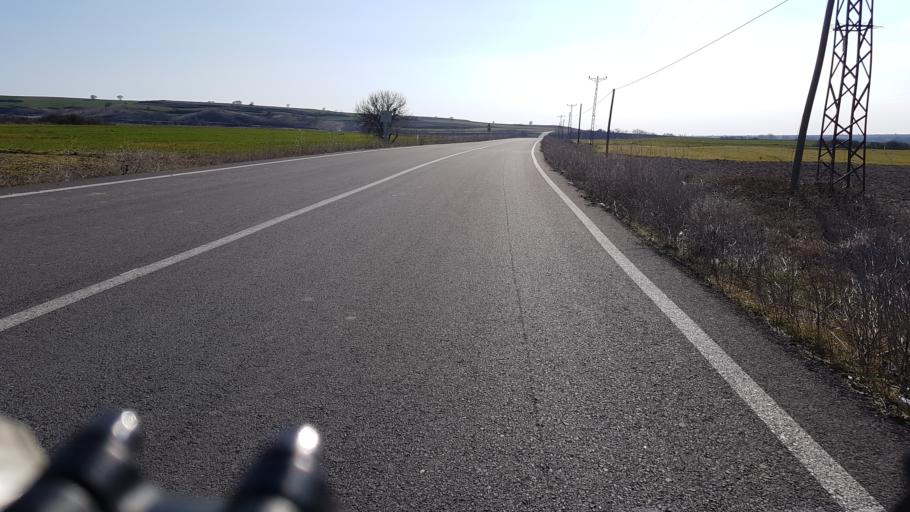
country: TR
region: Tekirdag
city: Saray
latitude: 41.3623
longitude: 27.8560
